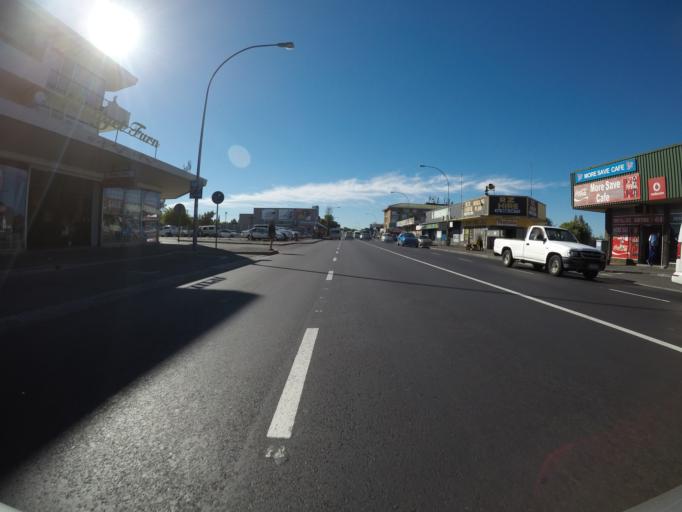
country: ZA
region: Western Cape
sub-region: City of Cape Town
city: Kraaifontein
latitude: -33.9223
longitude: 18.6766
